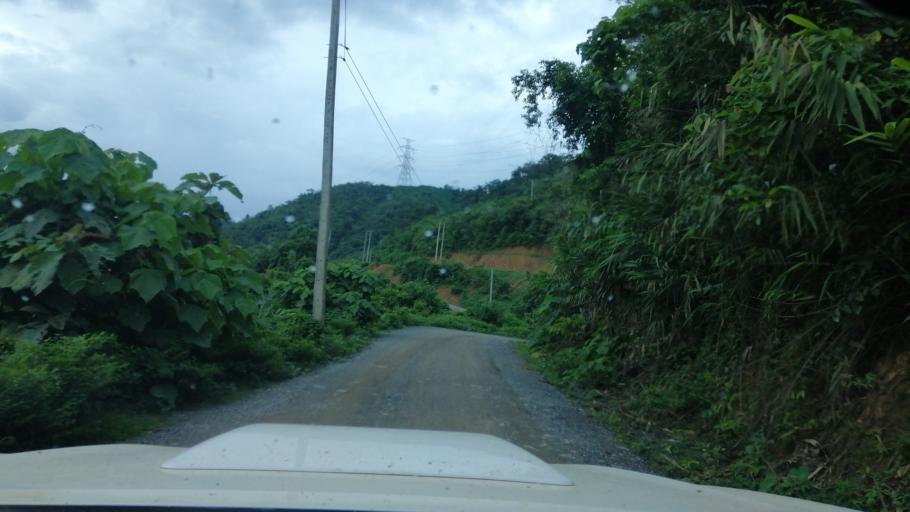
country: LA
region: Xiagnabouli
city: Sainyabuli
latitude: 19.1903
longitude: 101.7865
